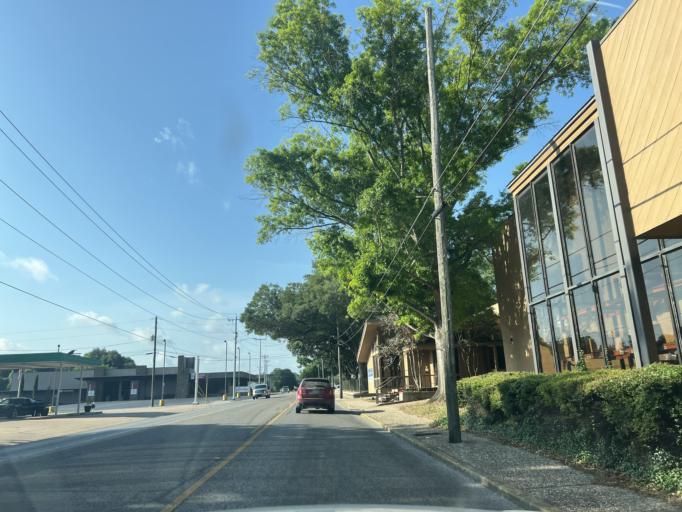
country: US
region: Texas
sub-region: Washington County
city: Brenham
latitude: 30.1545
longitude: -96.3926
